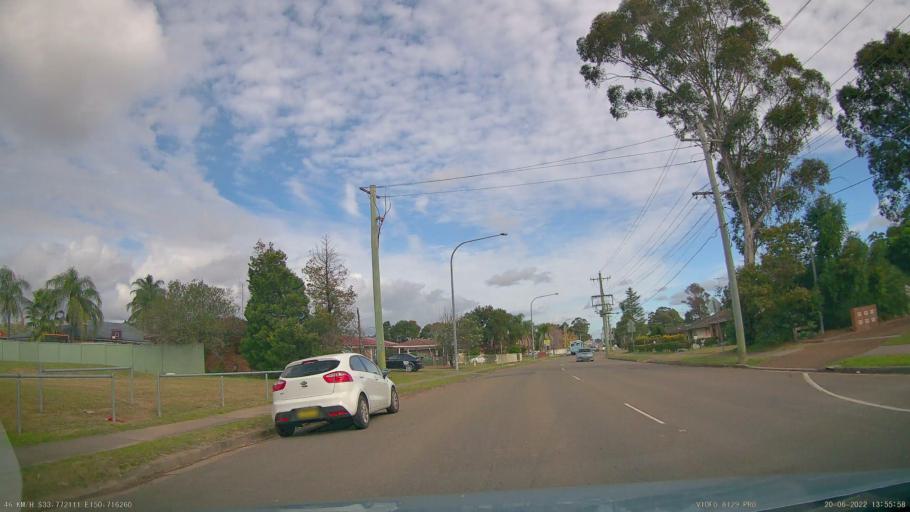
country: AU
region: New South Wales
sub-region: Penrith Municipality
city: Kingswood Park
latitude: -33.7722
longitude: 150.7161
